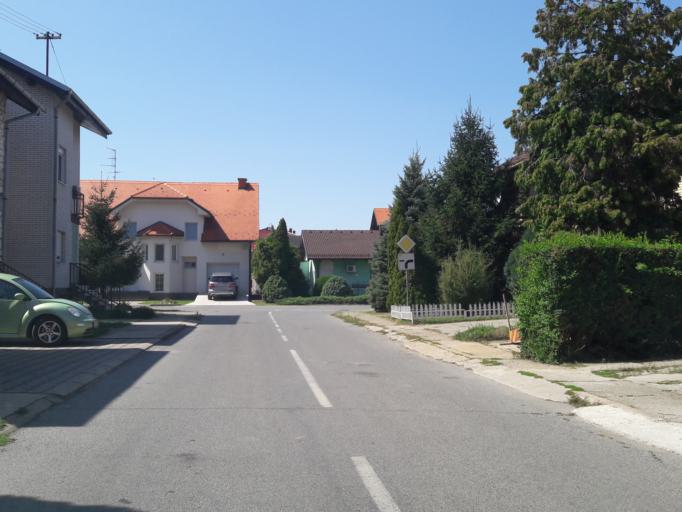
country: HR
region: Osjecko-Baranjska
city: Visnjevac
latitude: 45.5579
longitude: 18.6427
